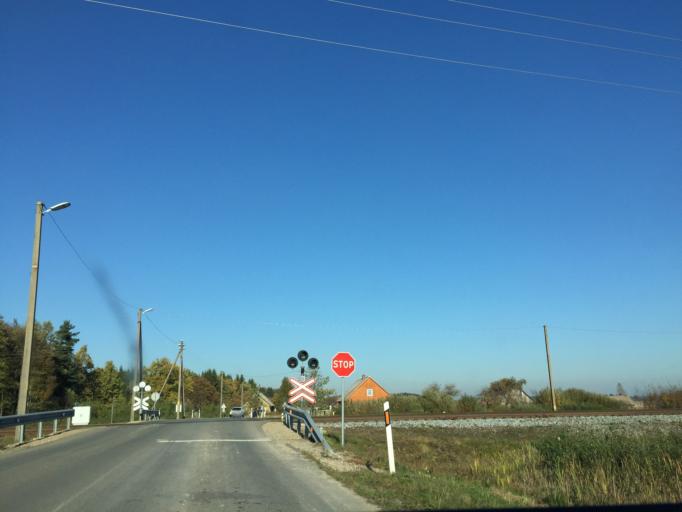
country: LT
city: Salantai
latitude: 55.9595
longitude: 21.6513
